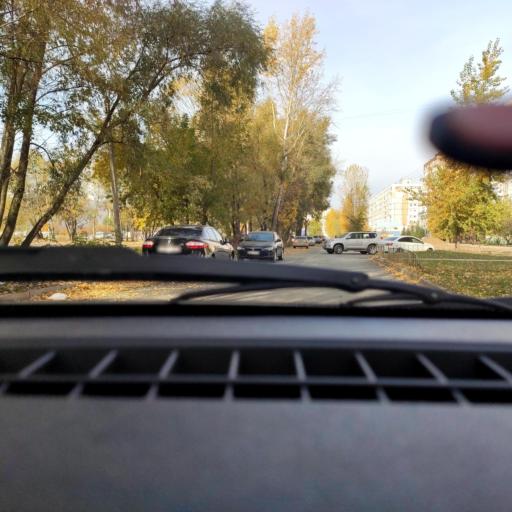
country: RU
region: Bashkortostan
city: Ufa
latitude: 54.7653
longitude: 56.0770
